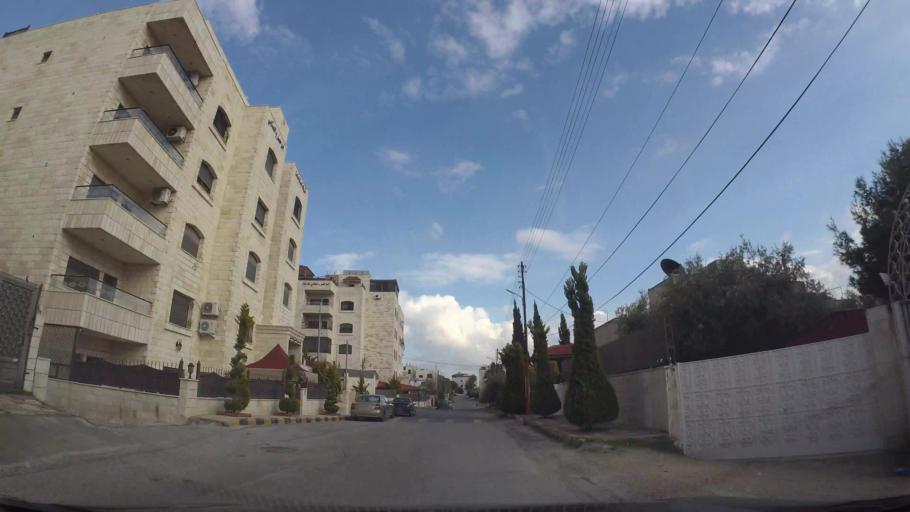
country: JO
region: Amman
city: Al Bunayyat ash Shamaliyah
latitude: 31.9099
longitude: 35.8840
